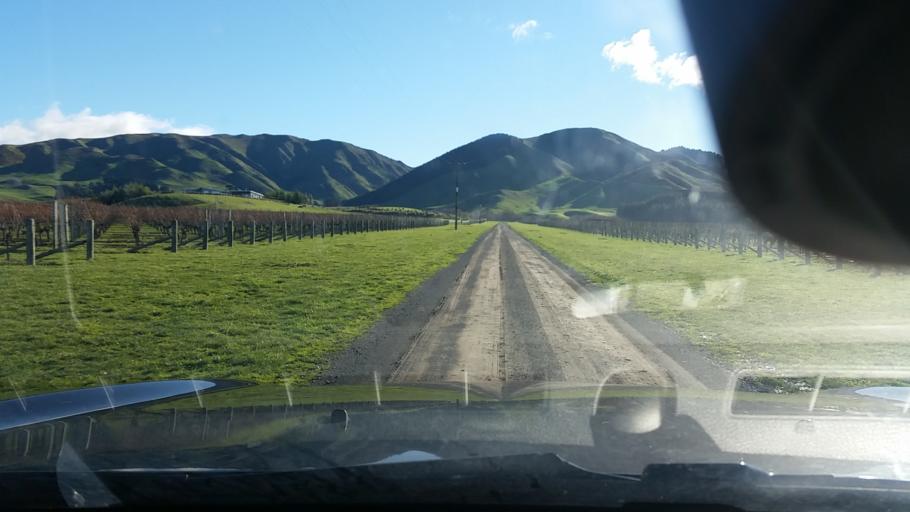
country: NZ
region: Marlborough
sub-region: Marlborough District
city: Blenheim
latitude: -41.6404
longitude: 174.0370
